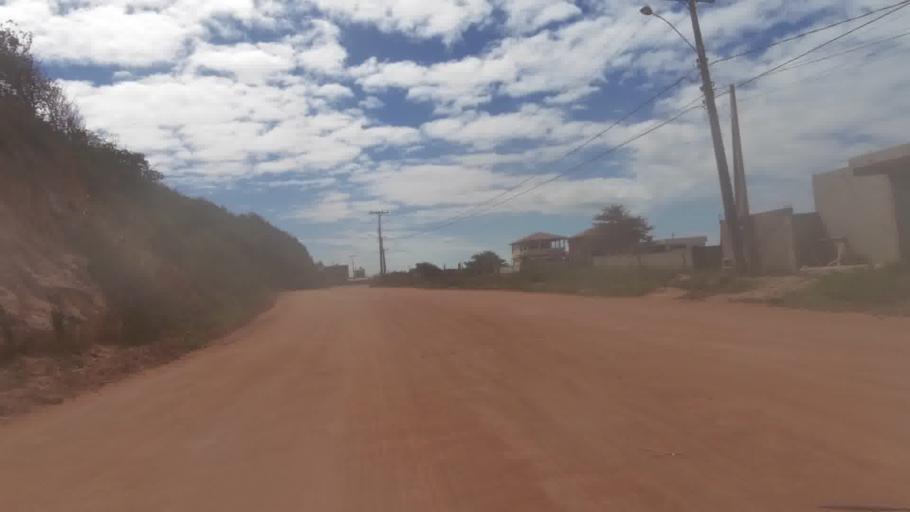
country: BR
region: Espirito Santo
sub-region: Marataizes
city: Marataizes
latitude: -21.1891
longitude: -40.9273
